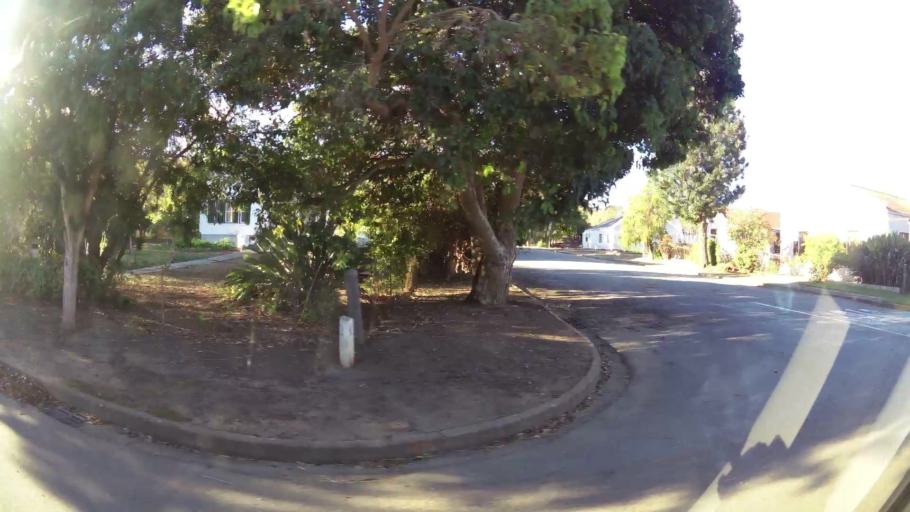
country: ZA
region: Western Cape
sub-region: Eden District Municipality
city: Riversdale
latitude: -34.0878
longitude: 20.9541
